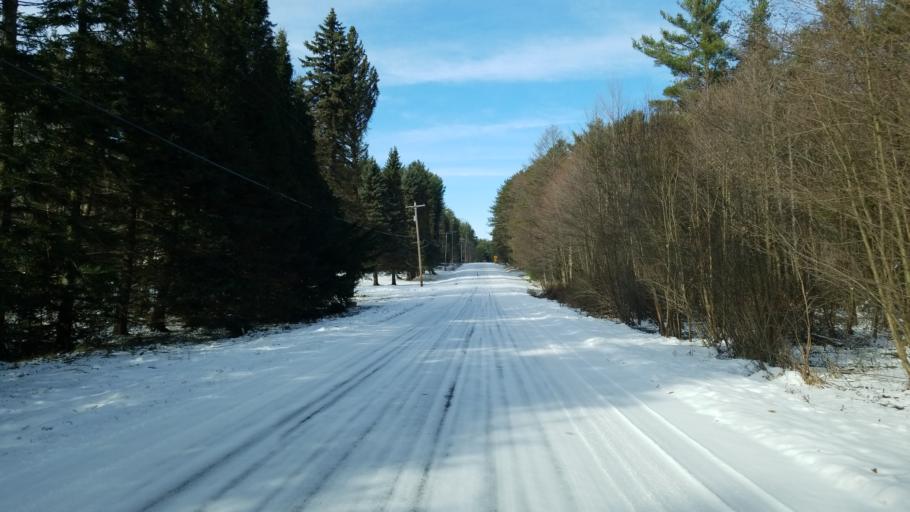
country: US
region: Pennsylvania
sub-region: Clearfield County
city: Clearfield
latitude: 41.1192
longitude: -78.5303
